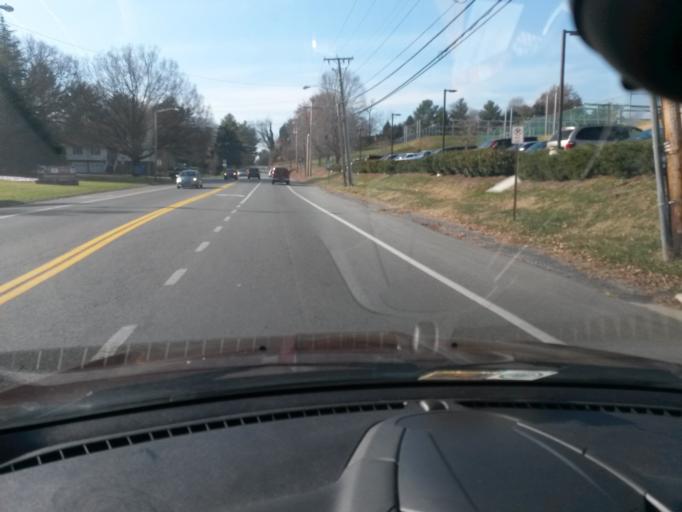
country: US
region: Virginia
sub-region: City of Roanoke
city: Roanoke
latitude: 37.2459
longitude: -79.9738
